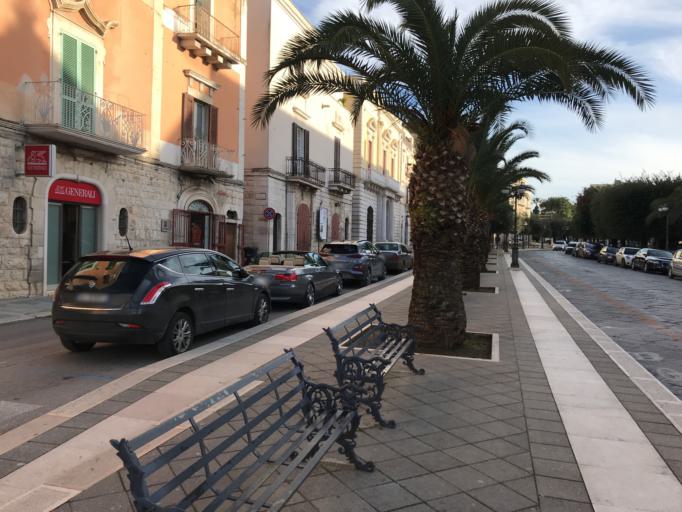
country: IT
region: Apulia
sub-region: Provincia di Bari
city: Corato
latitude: 41.1533
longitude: 16.4133
